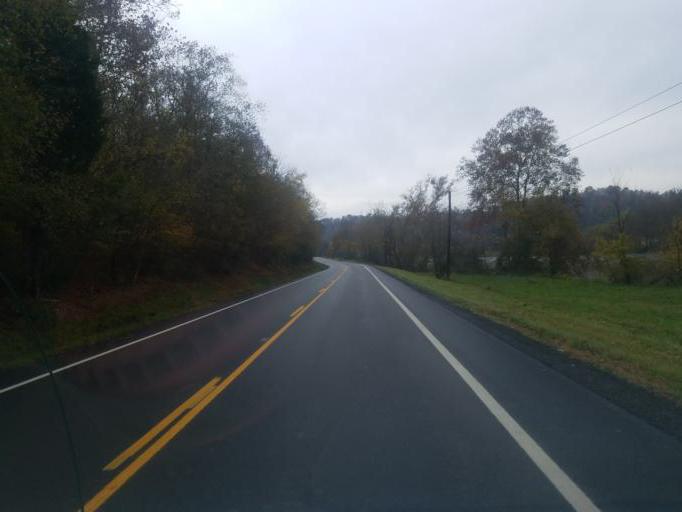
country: US
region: Ohio
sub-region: Washington County
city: Beverly
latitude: 39.5401
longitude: -81.5463
